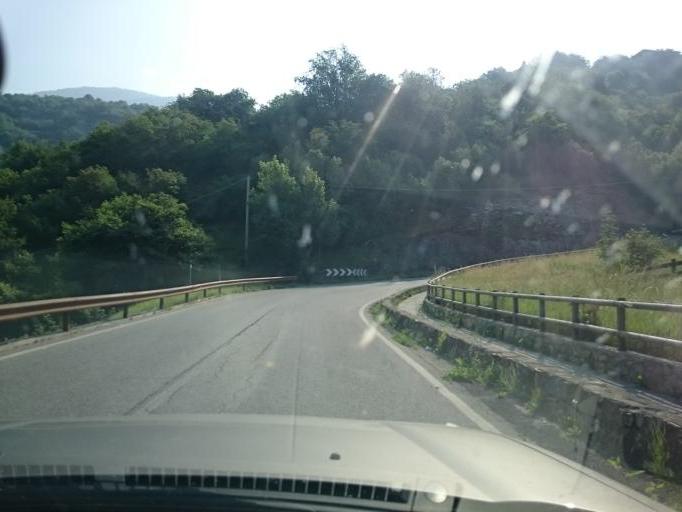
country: IT
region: Lombardy
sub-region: Provincia di Brescia
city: Cimbergo
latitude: 46.0267
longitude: 10.3618
